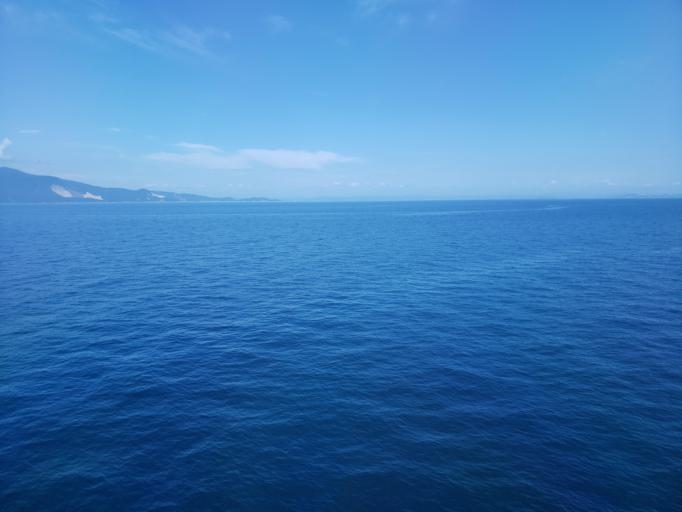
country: JP
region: Kagawa
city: Tonosho
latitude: 34.4505
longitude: 134.4325
